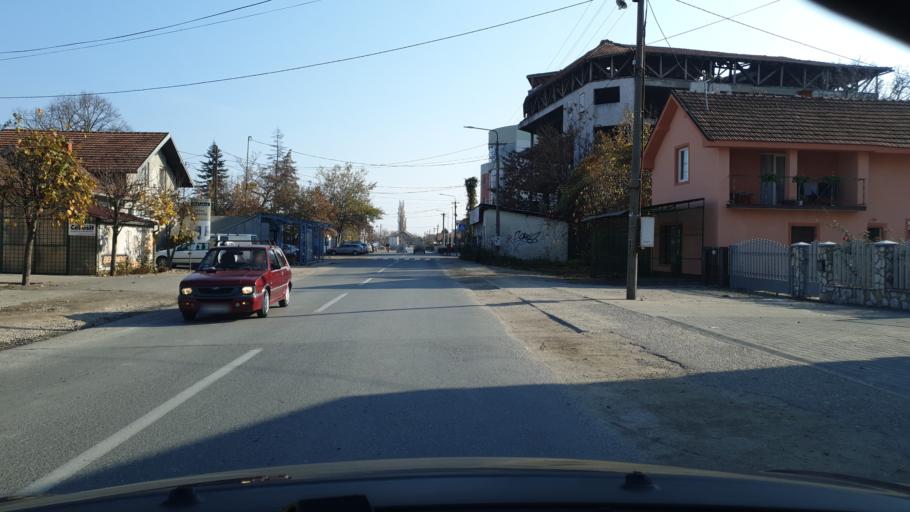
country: RS
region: Central Serbia
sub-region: Borski Okrug
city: Negotin
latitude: 44.2289
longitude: 22.5389
